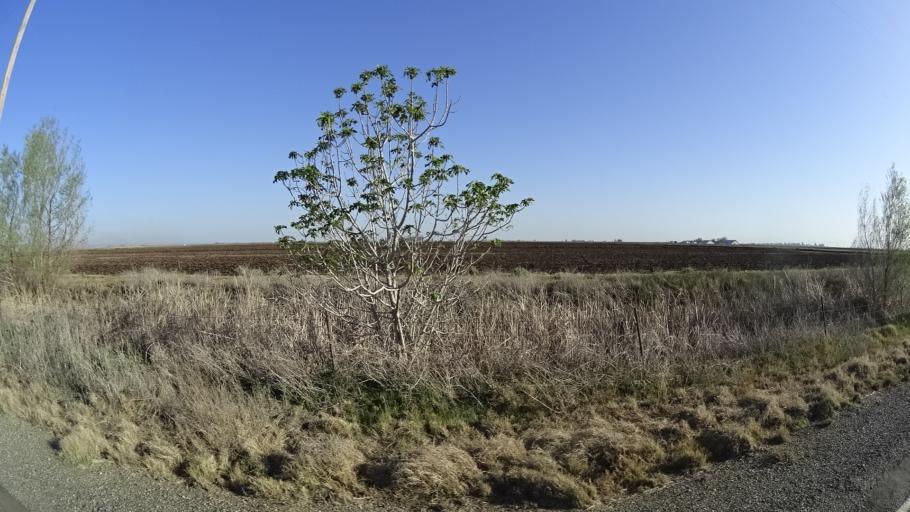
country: US
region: California
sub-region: Glenn County
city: Willows
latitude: 39.4071
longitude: -122.2194
